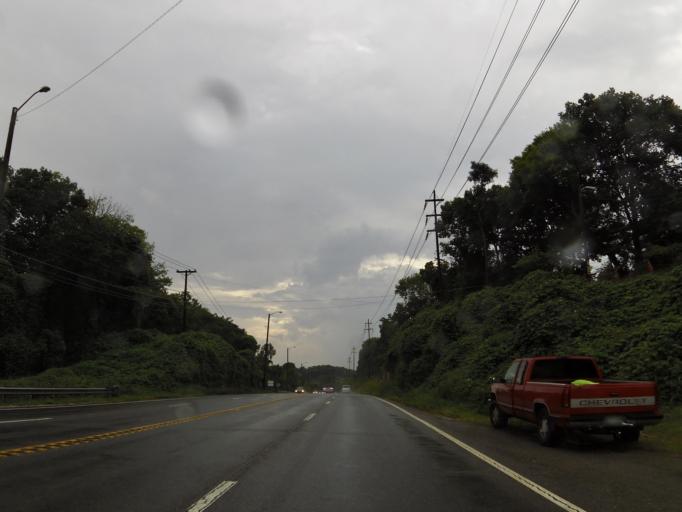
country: US
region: Tennessee
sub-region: Knox County
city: Knoxville
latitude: 35.9154
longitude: -83.8566
